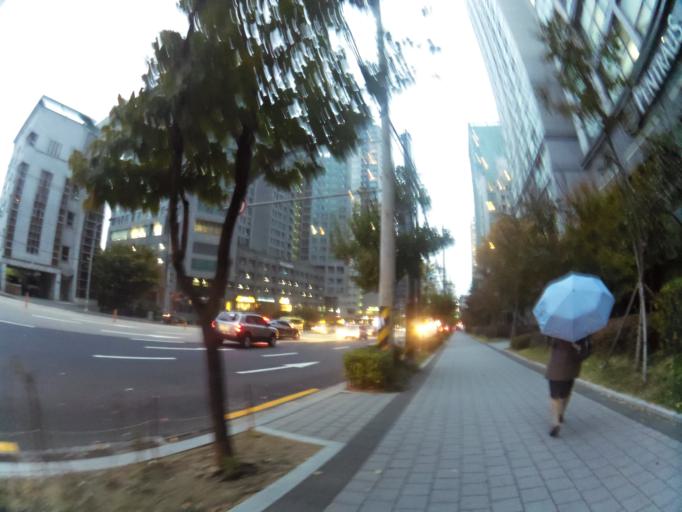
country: KR
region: Seoul
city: Seoul
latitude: 37.5425
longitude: 126.9547
